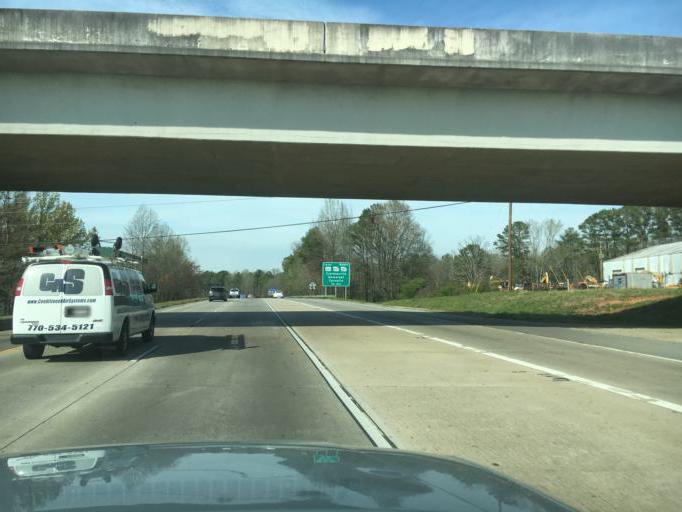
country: US
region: Georgia
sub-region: Habersham County
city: Cornelia
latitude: 34.5222
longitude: -83.5425
